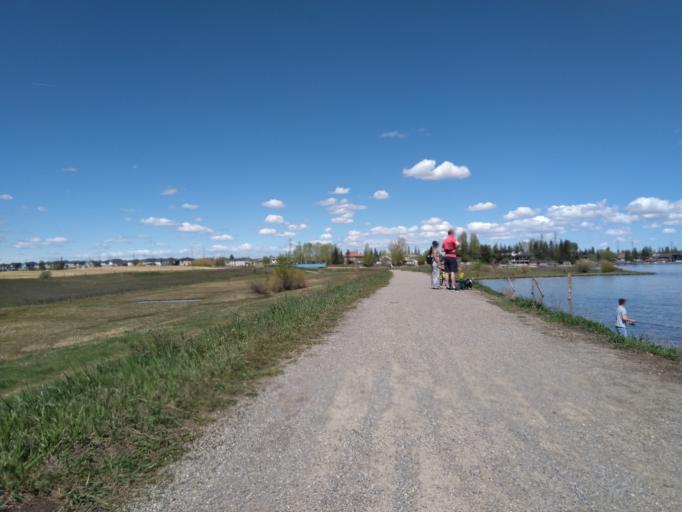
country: CA
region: Alberta
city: Chestermere
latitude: 51.0183
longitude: -113.8243
